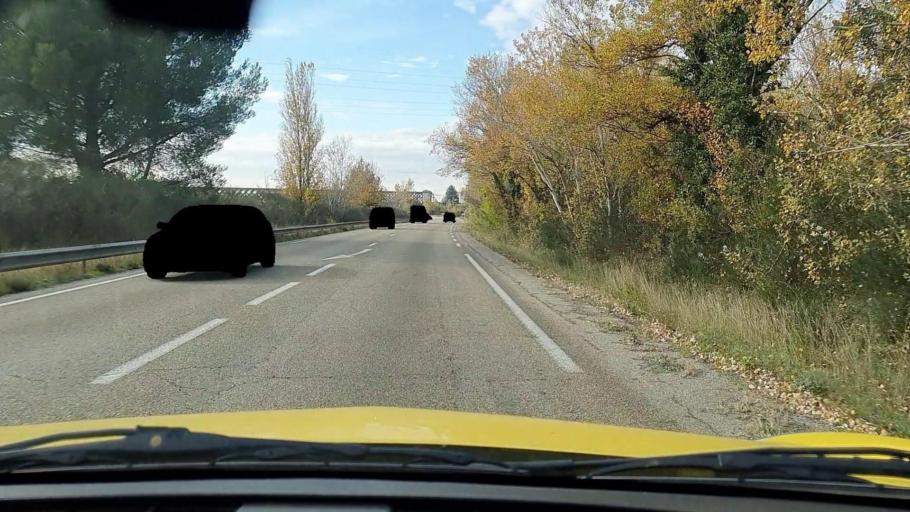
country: FR
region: Languedoc-Roussillon
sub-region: Departement du Gard
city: Les Angles
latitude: 43.9450
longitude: 4.7832
